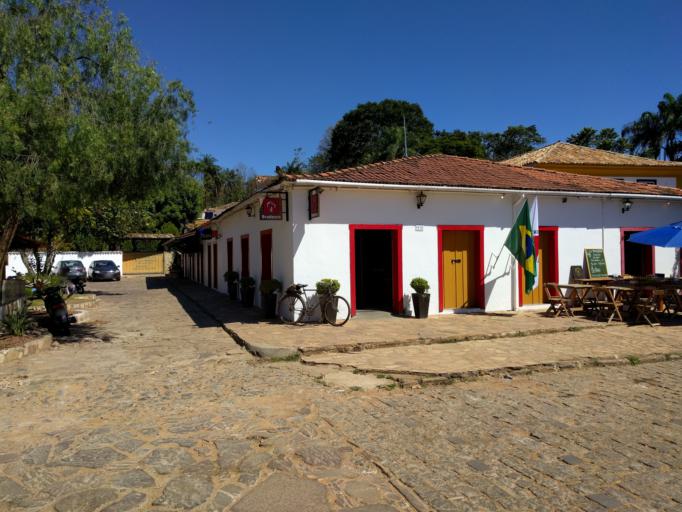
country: BR
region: Minas Gerais
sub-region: Tiradentes
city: Tiradentes
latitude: -21.1100
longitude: -44.1746
